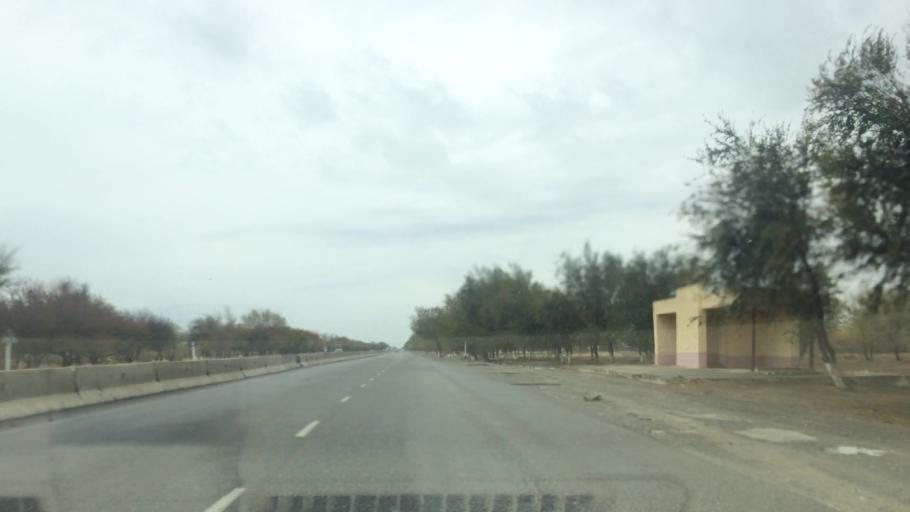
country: UZ
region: Samarqand
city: Bulung'ur
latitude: 39.8372
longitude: 67.4275
